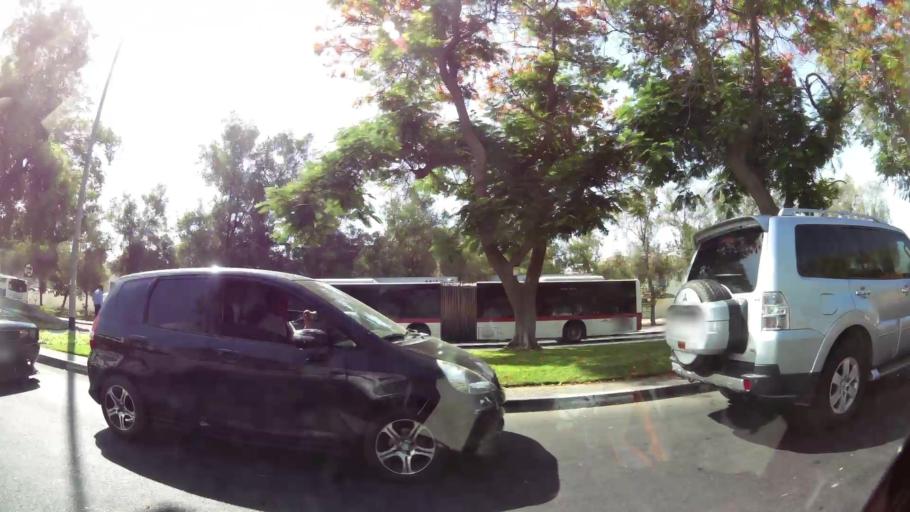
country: AE
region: Ash Shariqah
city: Sharjah
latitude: 25.2477
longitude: 55.2860
